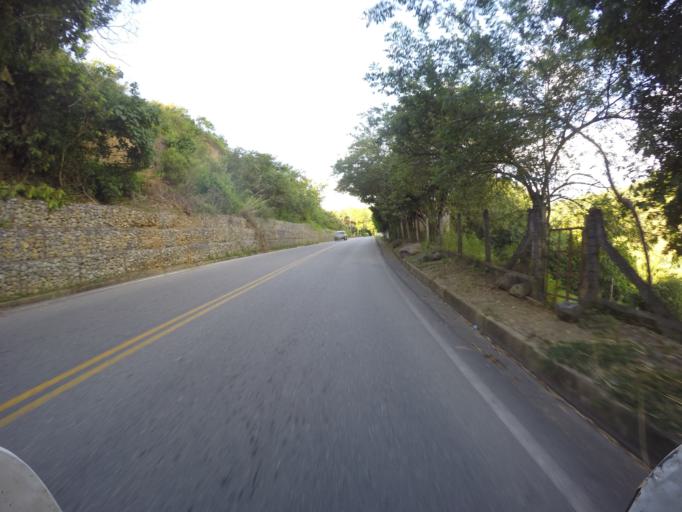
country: CO
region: Valle del Cauca
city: Alcala
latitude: 4.7043
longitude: -75.8483
